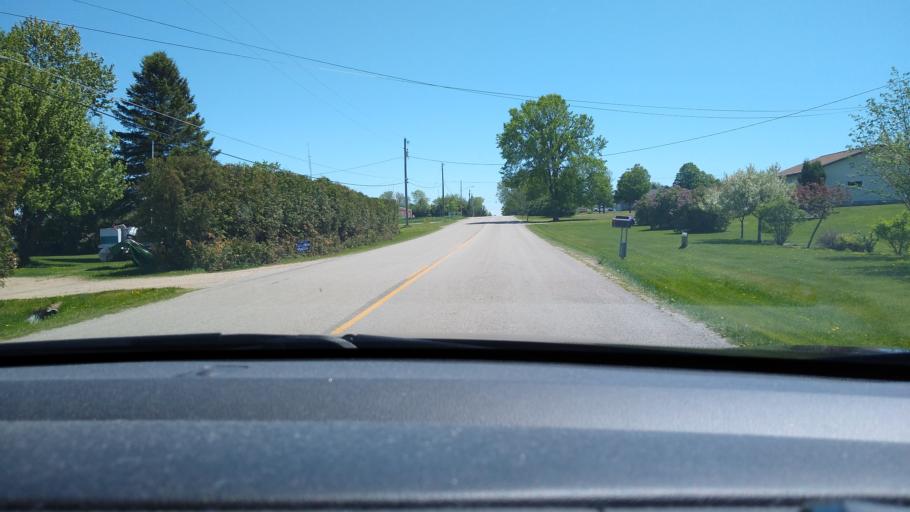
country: US
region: Michigan
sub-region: Delta County
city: Escanaba
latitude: 45.8260
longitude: -87.1743
